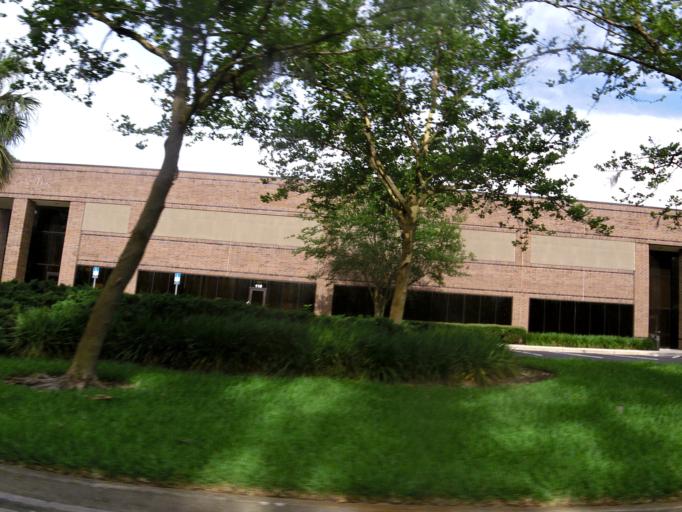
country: US
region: Florida
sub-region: Saint Johns County
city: Fruit Cove
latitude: 30.1833
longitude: -81.5496
